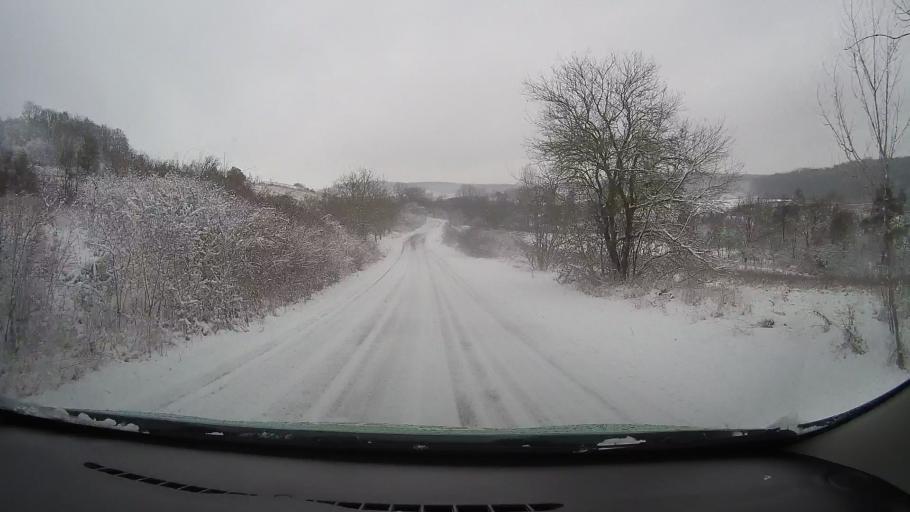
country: RO
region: Hunedoara
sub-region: Comuna Pestisu Mic
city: Pestisu Mic
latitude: 45.8184
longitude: 22.8813
